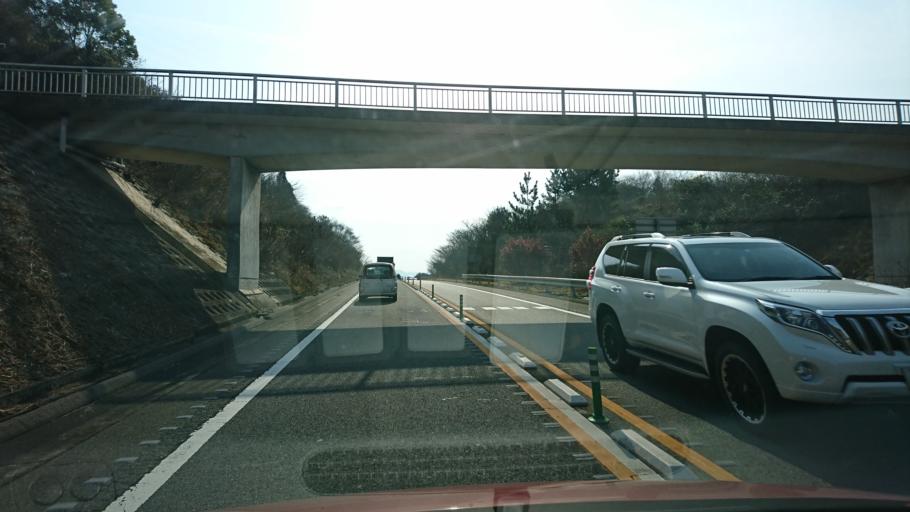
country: JP
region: Hiroshima
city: Onomichi
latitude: 34.3668
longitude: 133.1913
